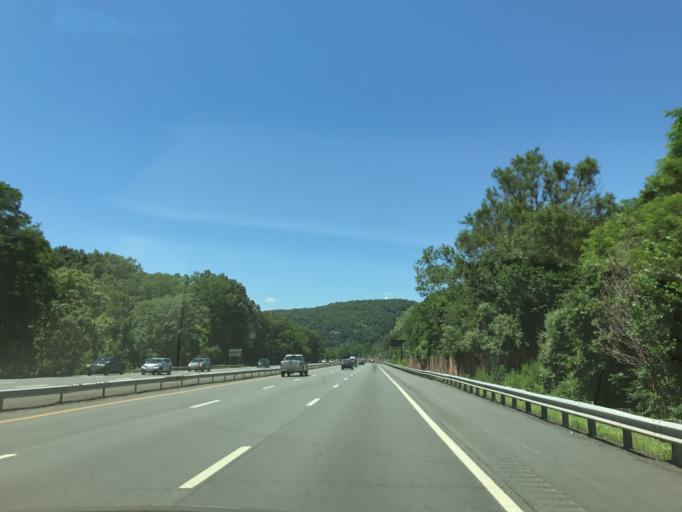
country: US
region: New York
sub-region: Rockland County
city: Montebello
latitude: 41.1200
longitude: -74.1282
